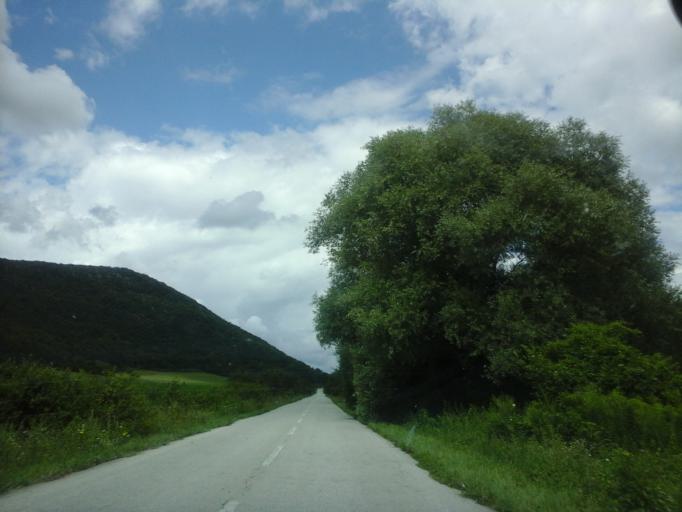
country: SK
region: Kosicky
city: Roznava
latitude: 48.5627
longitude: 20.3958
